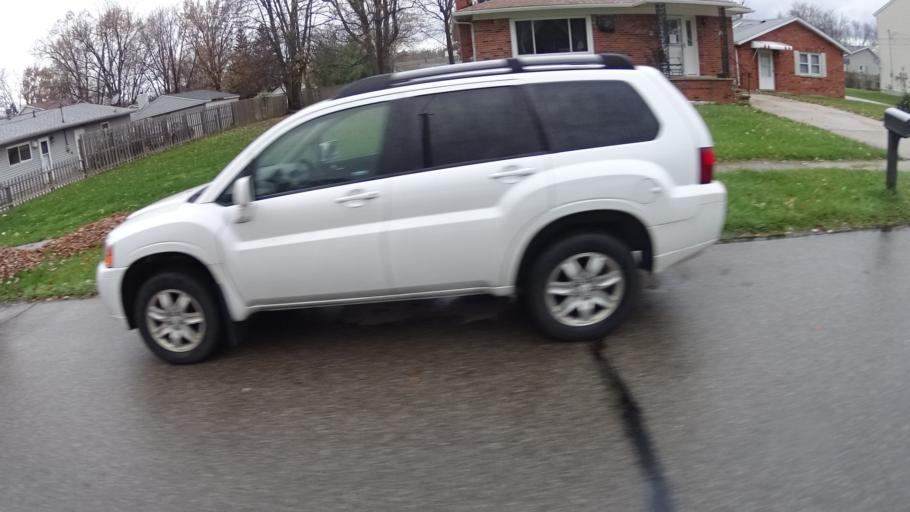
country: US
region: Ohio
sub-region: Lorain County
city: Elyria
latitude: 41.3892
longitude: -82.1276
